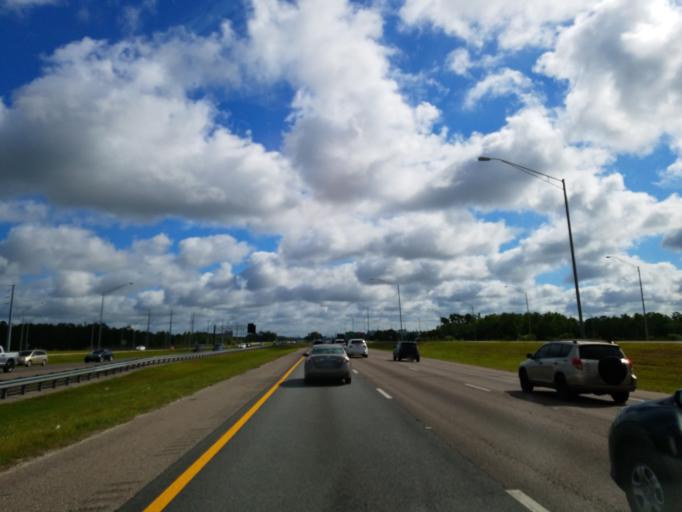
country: US
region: Florida
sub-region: Osceola County
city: Celebration
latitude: 28.3070
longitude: -81.5694
